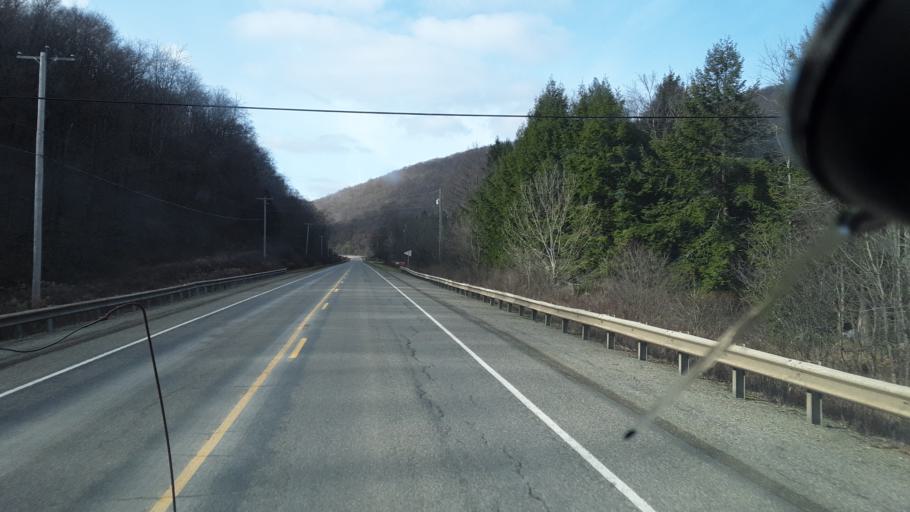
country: US
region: Pennsylvania
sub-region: Potter County
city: Galeton
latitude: 41.7807
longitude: -77.8099
